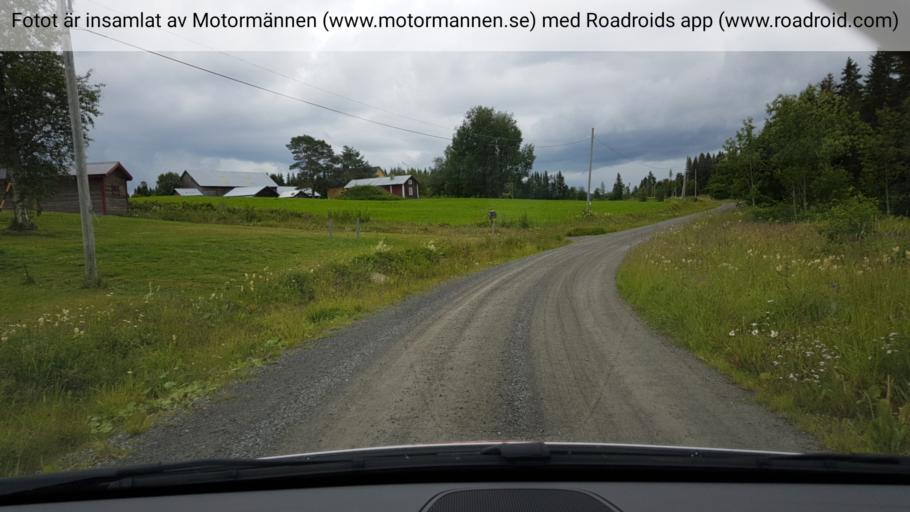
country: SE
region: Jaemtland
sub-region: Krokoms Kommun
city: Valla
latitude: 63.5267
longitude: 13.8856
